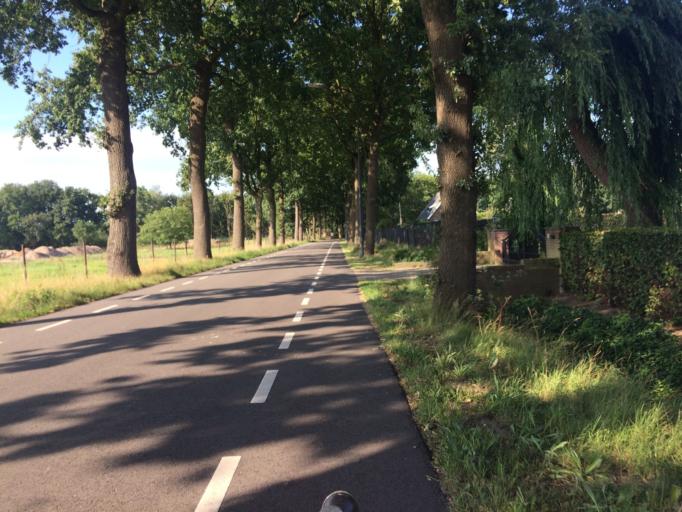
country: NL
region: North Brabant
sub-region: Gemeente Vught
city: Vught
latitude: 51.6648
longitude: 5.2328
